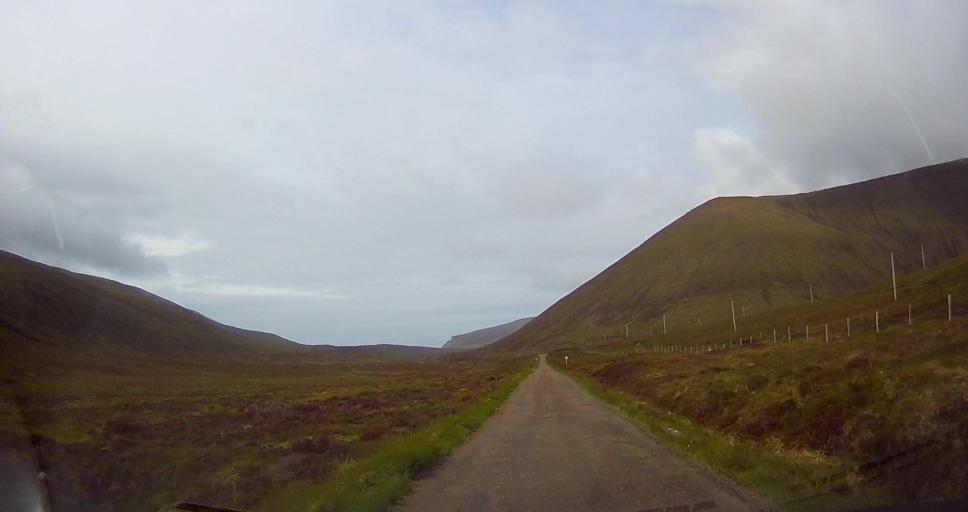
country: GB
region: Scotland
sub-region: Orkney Islands
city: Stromness
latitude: 58.8874
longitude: -3.3206
